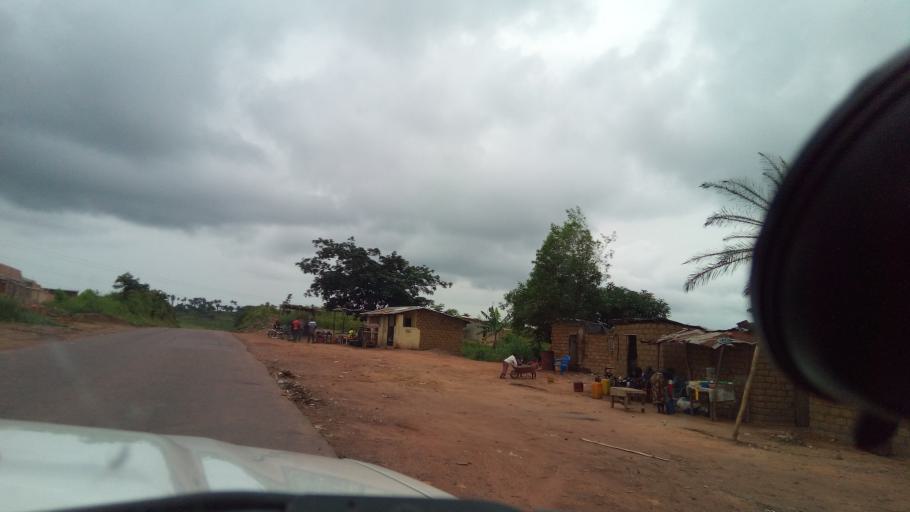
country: CD
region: Bas-Congo
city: Kasangulu
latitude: -4.9417
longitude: 15.1504
